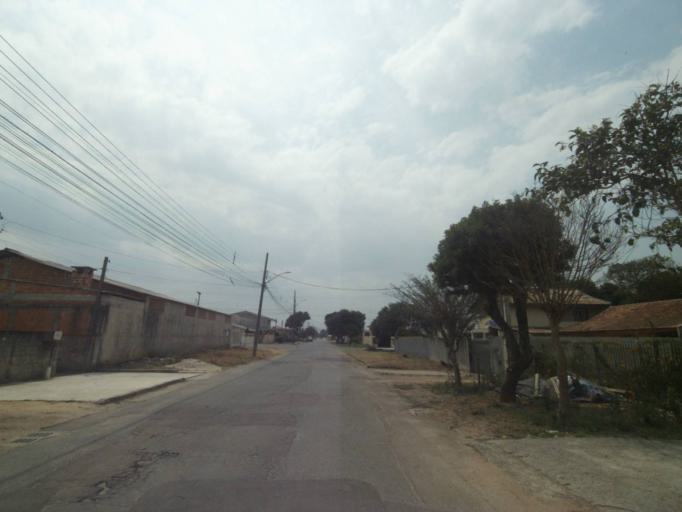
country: BR
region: Parana
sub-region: Pinhais
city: Pinhais
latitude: -25.4859
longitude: -49.1957
